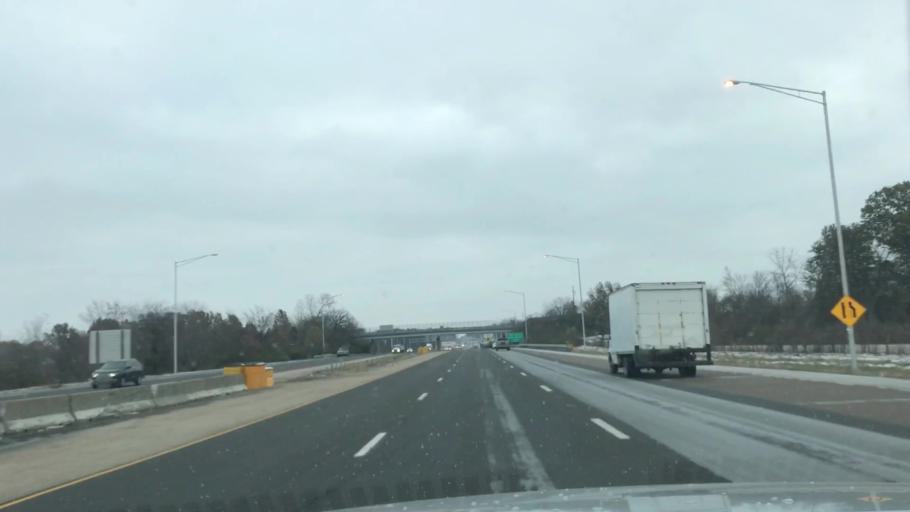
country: US
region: Illinois
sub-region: Madison County
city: Glen Carbon
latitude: 38.7568
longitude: -90.0288
